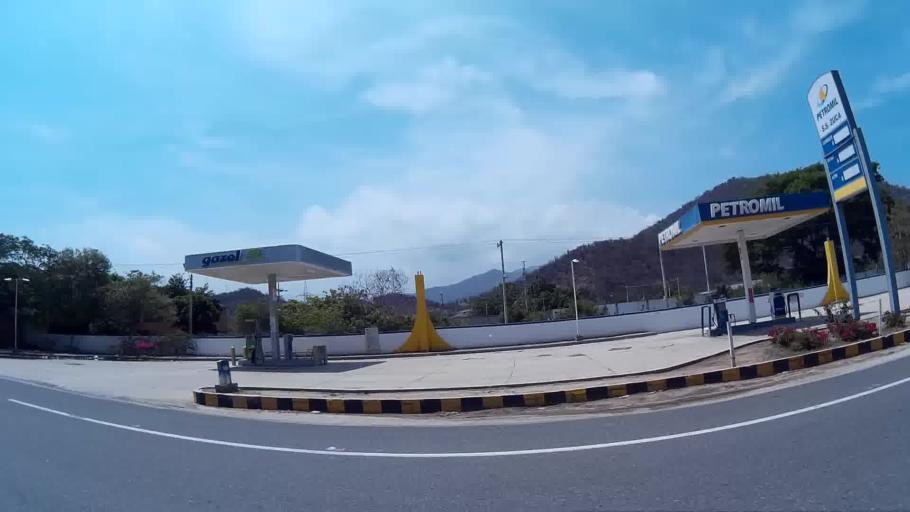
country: CO
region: Magdalena
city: Santa Marta
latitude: 11.1786
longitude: -74.2287
